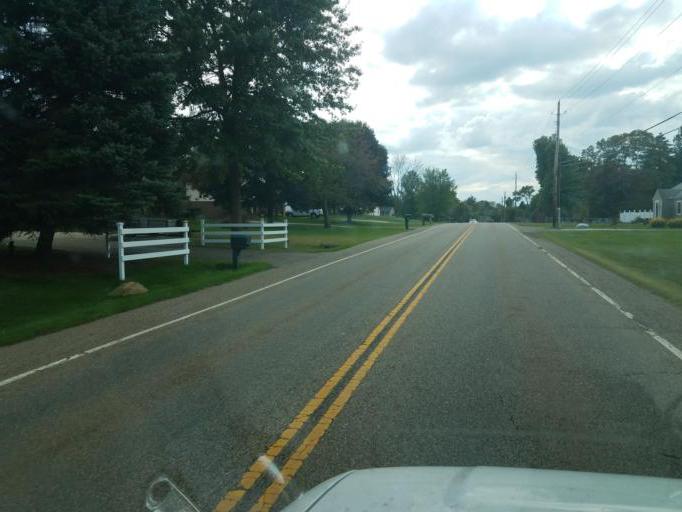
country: US
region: Ohio
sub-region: Stark County
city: Louisville
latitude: 40.8257
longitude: -81.2657
